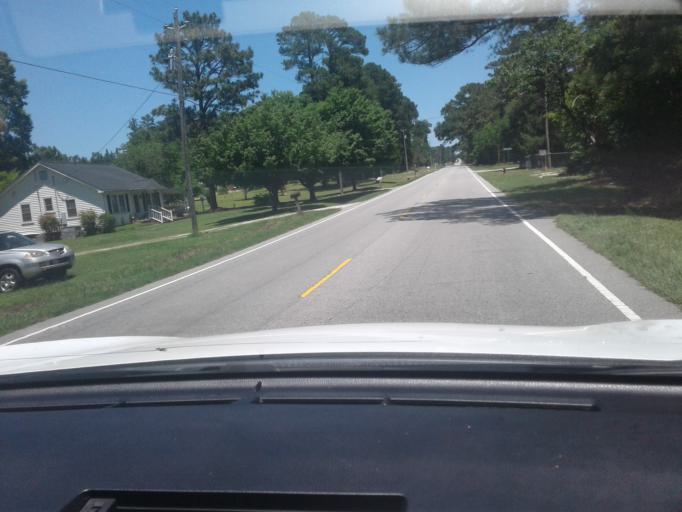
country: US
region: North Carolina
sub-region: Harnett County
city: Lillington
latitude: 35.3834
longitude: -78.8424
